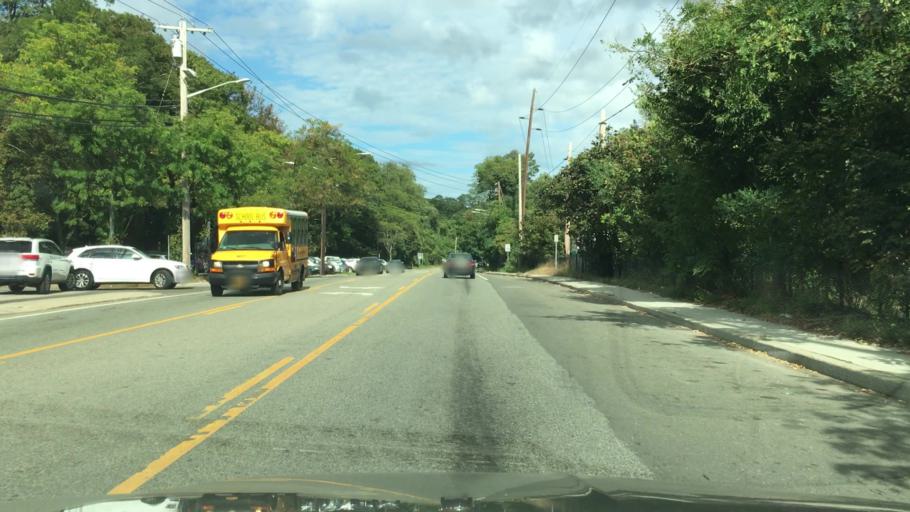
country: US
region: New York
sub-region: Suffolk County
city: Stony Brook
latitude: 40.9227
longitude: -73.1269
